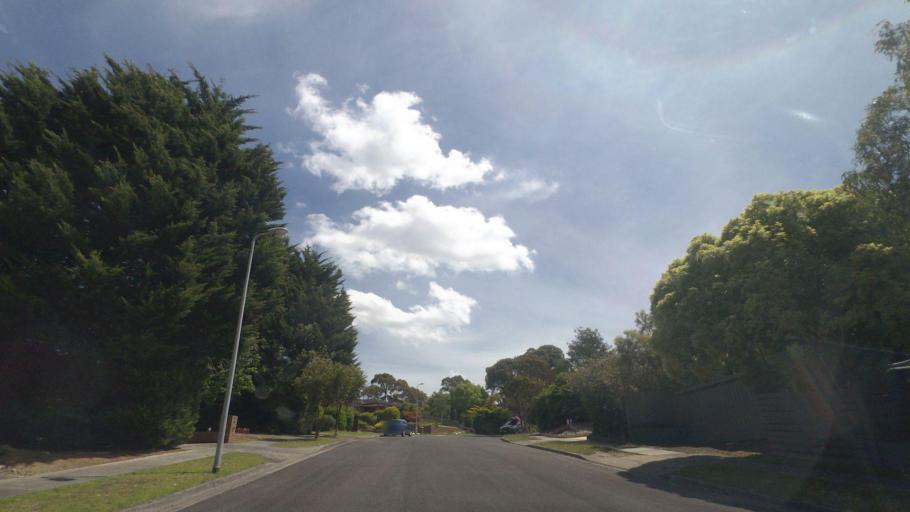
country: AU
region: Victoria
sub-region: Maroondah
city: Bayswater North
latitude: -37.8430
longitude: 145.2965
